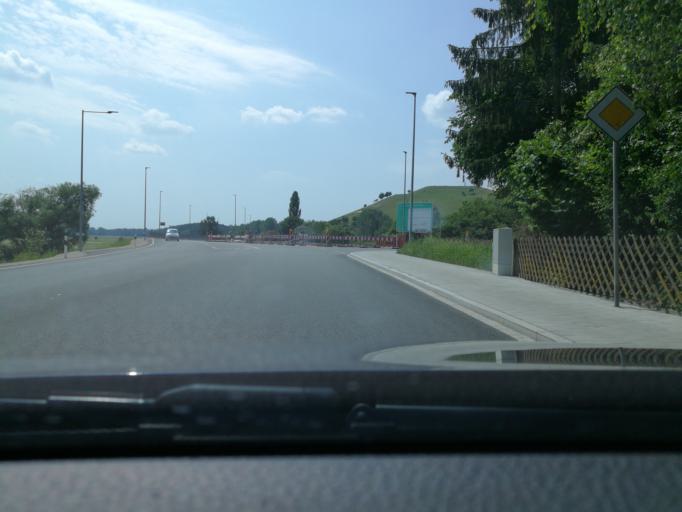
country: DE
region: Bavaria
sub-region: Regierungsbezirk Mittelfranken
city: Furth
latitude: 49.5154
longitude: 10.9640
